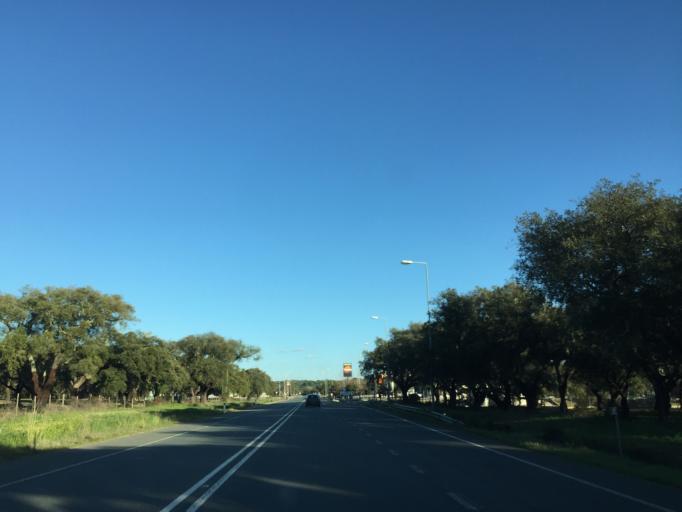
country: PT
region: Setubal
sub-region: Grandola
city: Grandola
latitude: 38.1219
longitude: -8.4494
